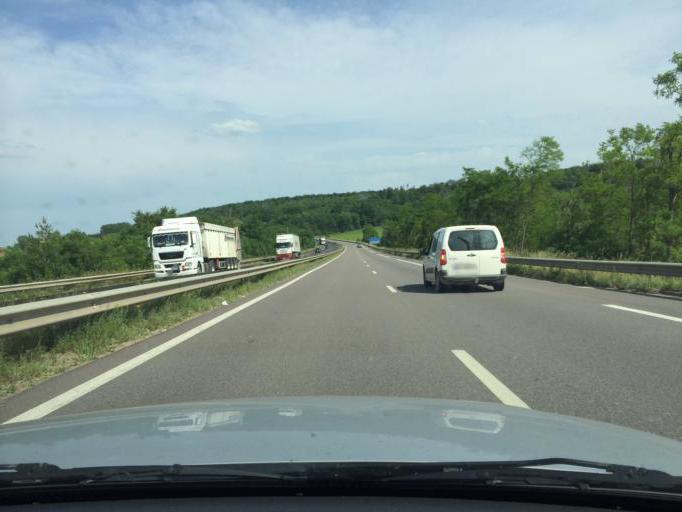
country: FR
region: Lorraine
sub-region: Departement de Meurthe-et-Moselle
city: Foug
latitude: 48.6722
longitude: 5.7764
